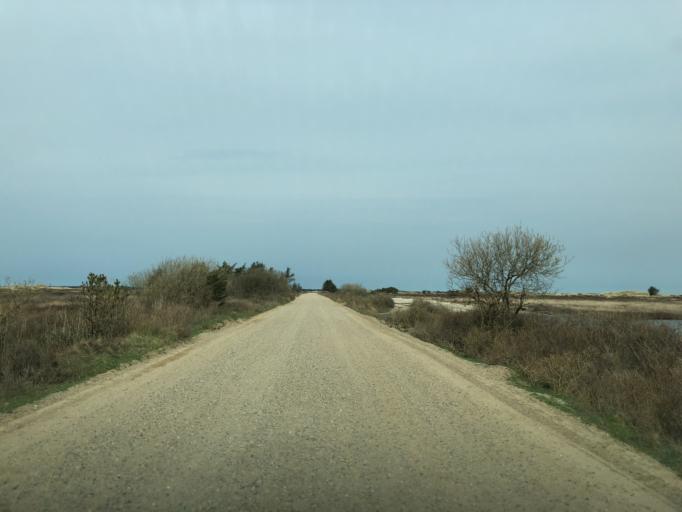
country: DK
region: South Denmark
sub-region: Varde Kommune
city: Oksbol
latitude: 55.5692
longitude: 8.1370
